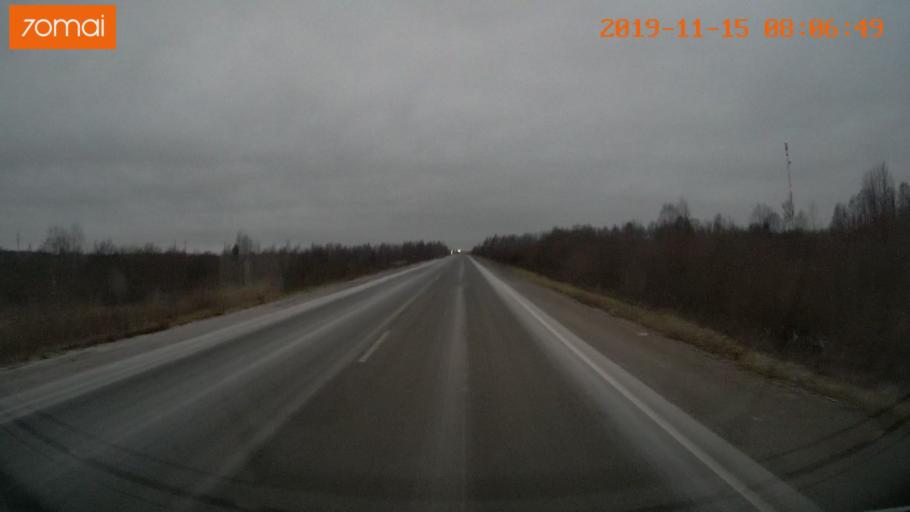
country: RU
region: Vologda
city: Cherepovets
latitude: 59.0238
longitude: 38.0296
